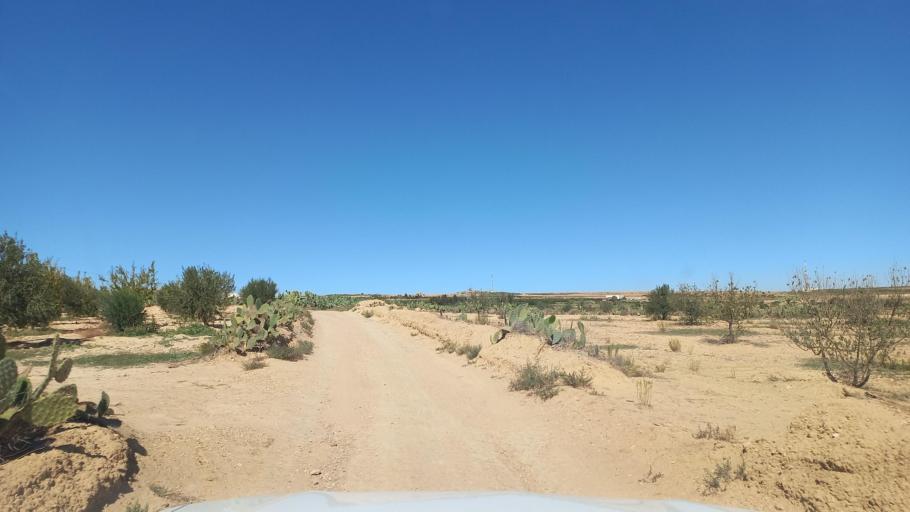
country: TN
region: Al Qasrayn
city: Sbiba
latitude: 35.3646
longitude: 9.0894
